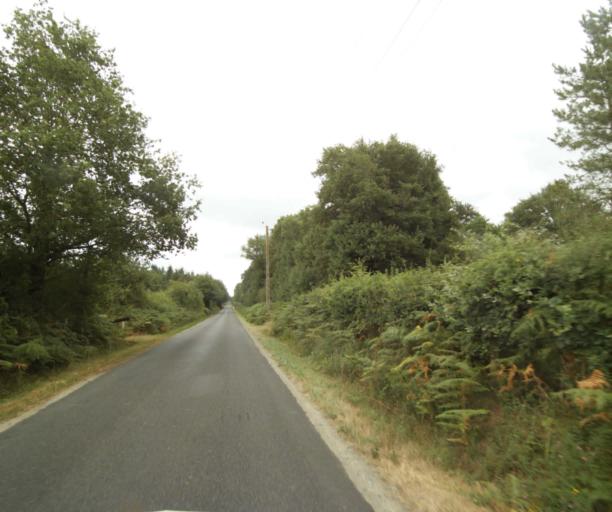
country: FR
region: Pays de la Loire
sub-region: Departement de la Sarthe
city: Sable-sur-Sarthe
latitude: 47.8063
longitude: -0.3627
